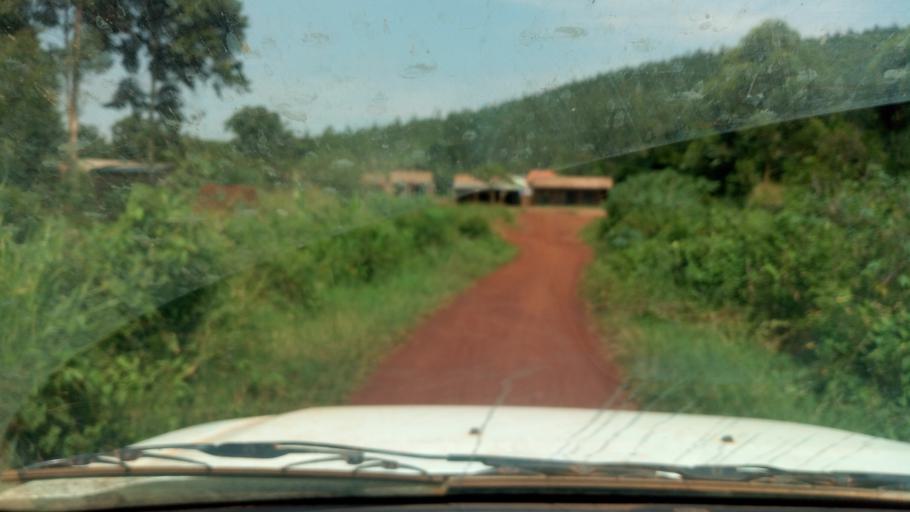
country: UG
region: Western Region
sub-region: Masindi District
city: Masindi
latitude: 1.6423
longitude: 31.8042
